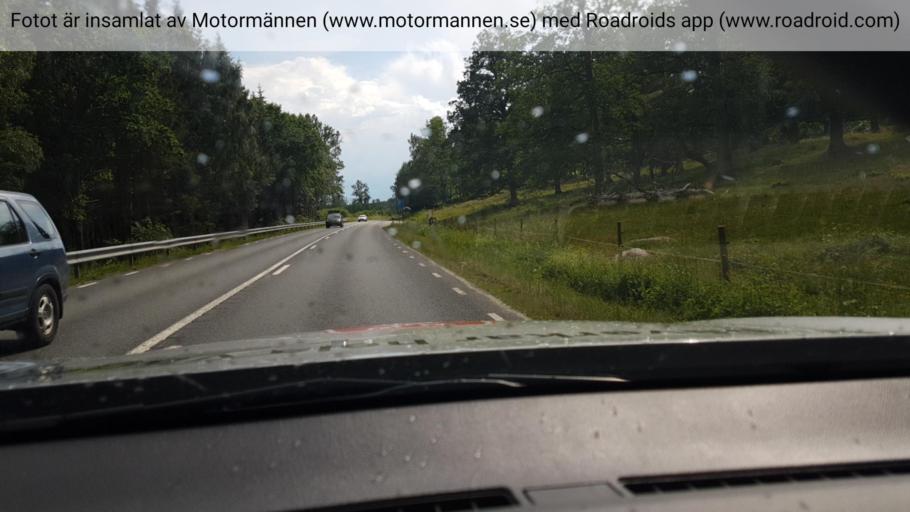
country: SE
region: Vaestra Goetaland
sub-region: Hjo Kommun
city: Hjo
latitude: 58.1236
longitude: 14.2176
